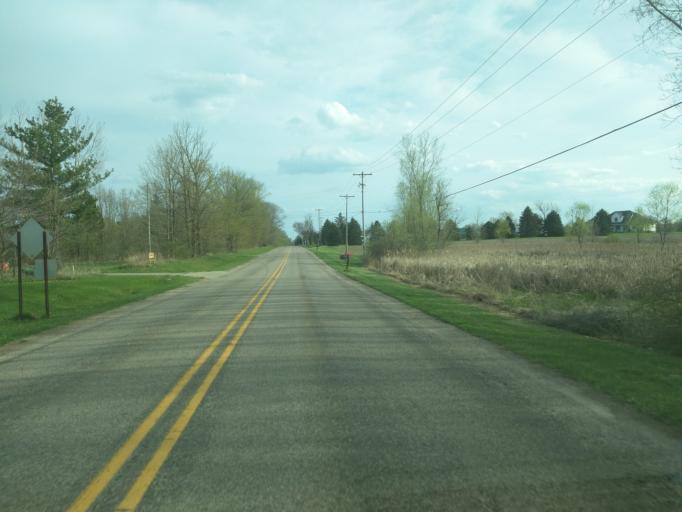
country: US
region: Michigan
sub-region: Eaton County
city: Dimondale
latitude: 42.6328
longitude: -84.6420
